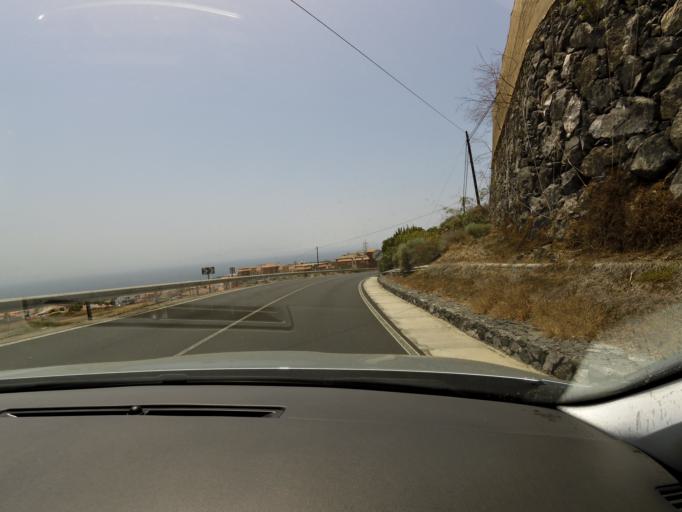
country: ES
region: Canary Islands
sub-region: Provincia de Santa Cruz de Tenerife
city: Adeje
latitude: 28.1335
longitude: -16.7747
